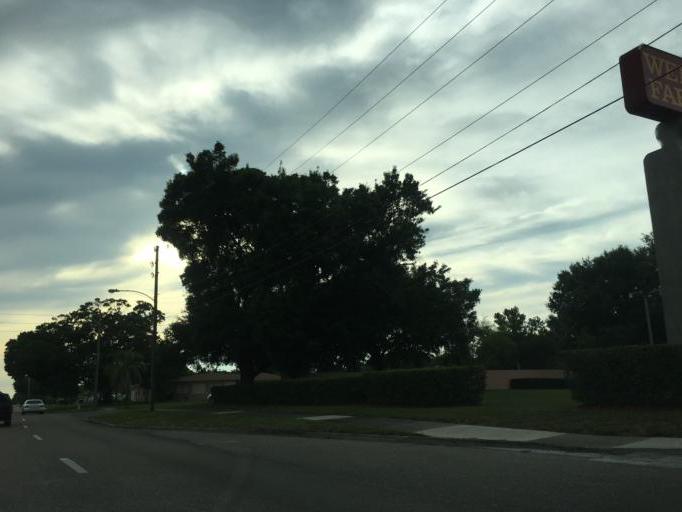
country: US
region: Florida
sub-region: Pinellas County
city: Saint Petersburg
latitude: 27.7919
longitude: -82.6808
